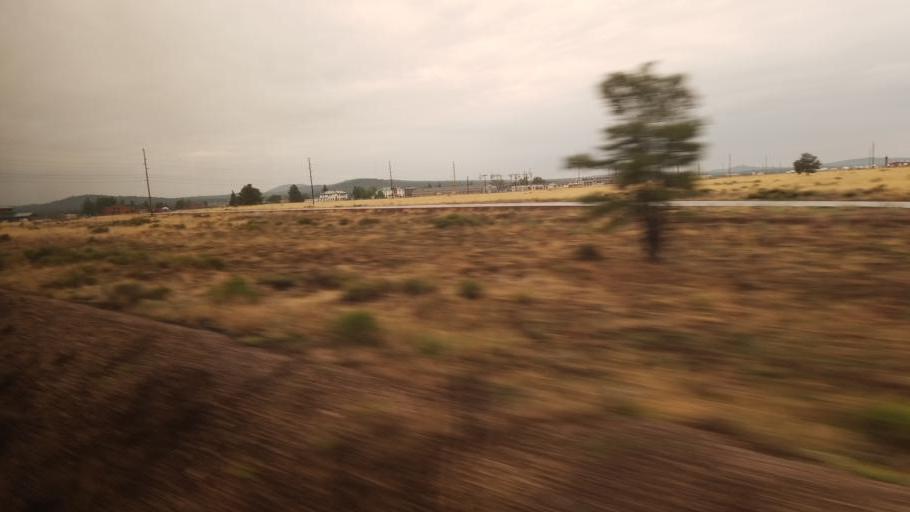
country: US
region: Arizona
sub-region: Coconino County
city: Parks
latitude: 35.2334
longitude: -111.8261
